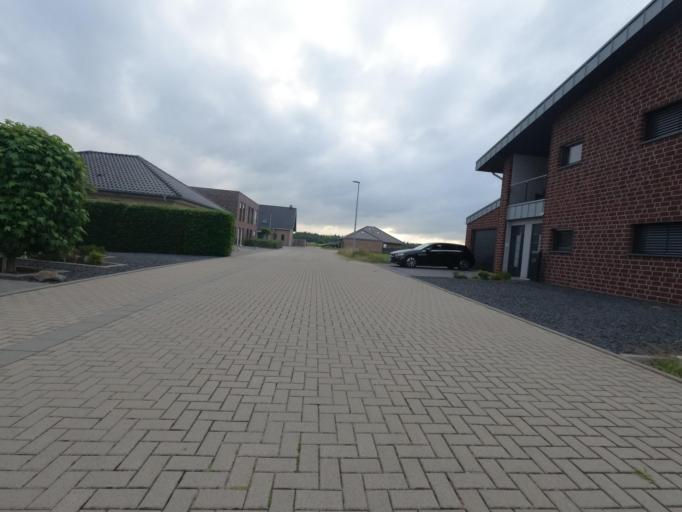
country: NL
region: Limburg
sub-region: Gemeente Roerdalen
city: Vlodrop
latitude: 51.1249
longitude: 6.1074
